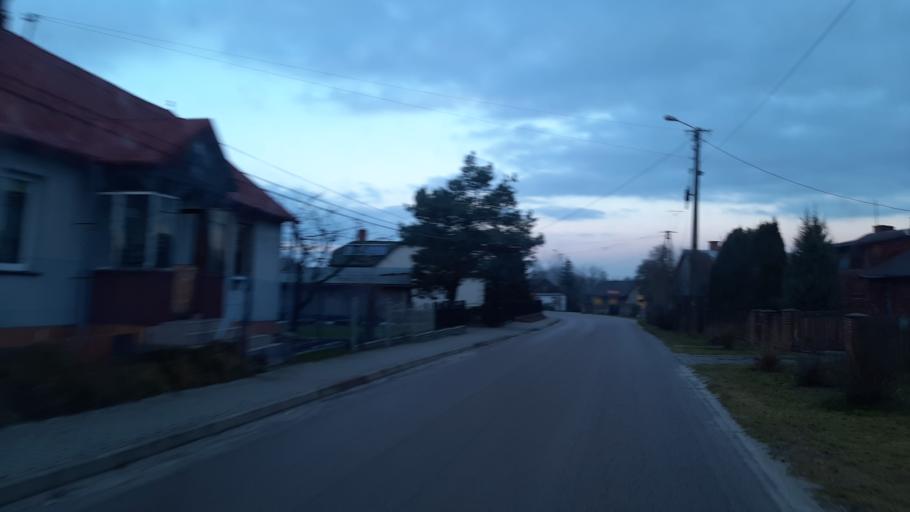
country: PL
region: Lublin Voivodeship
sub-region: Powiat lubartowski
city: Firlej
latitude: 51.5691
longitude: 22.5338
